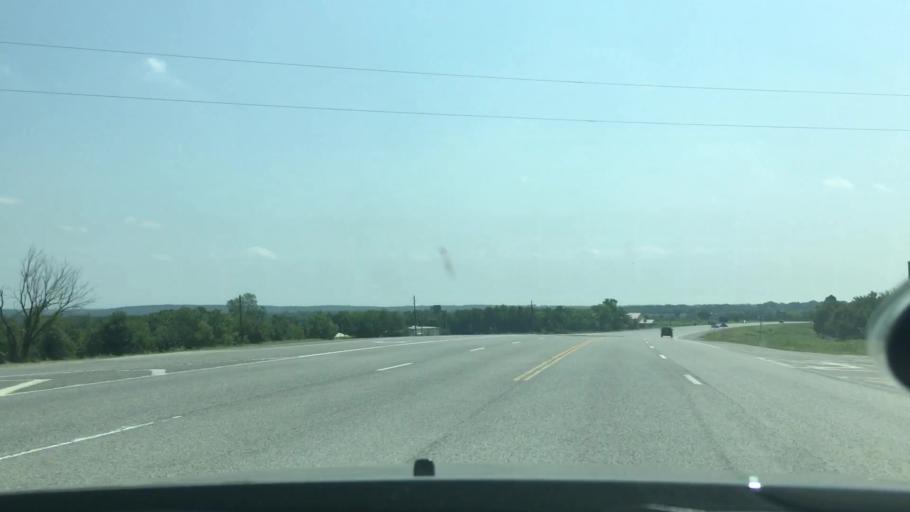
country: US
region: Oklahoma
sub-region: Atoka County
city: Atoka
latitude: 34.3730
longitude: -96.1106
